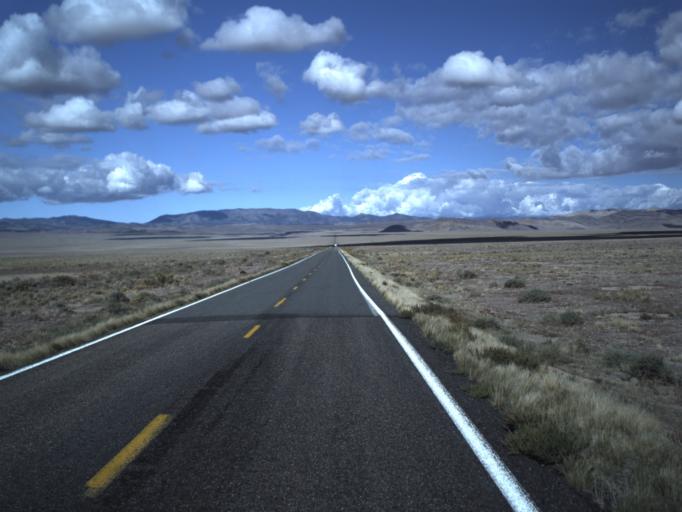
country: US
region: Utah
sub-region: Beaver County
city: Milford
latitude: 38.5361
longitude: -113.6920
